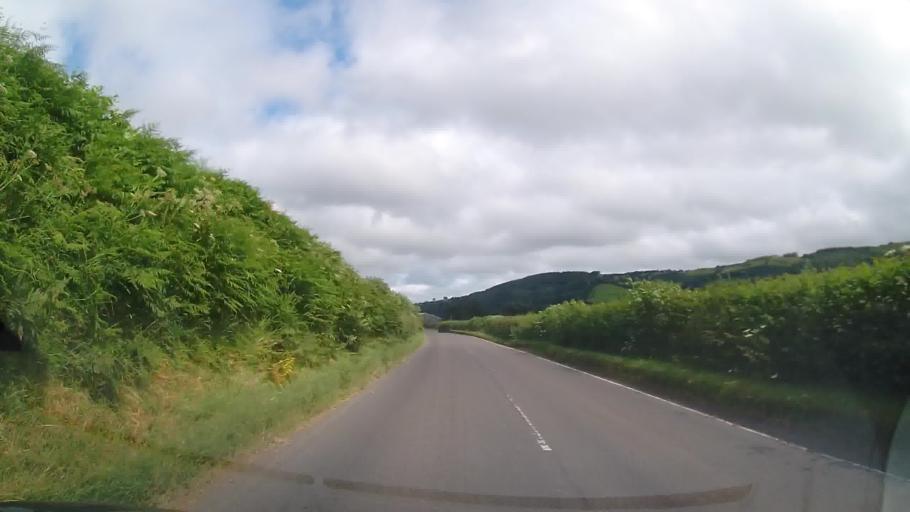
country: GB
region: Wales
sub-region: Sir Powys
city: Llanfechain
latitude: 52.8106
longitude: -3.2310
